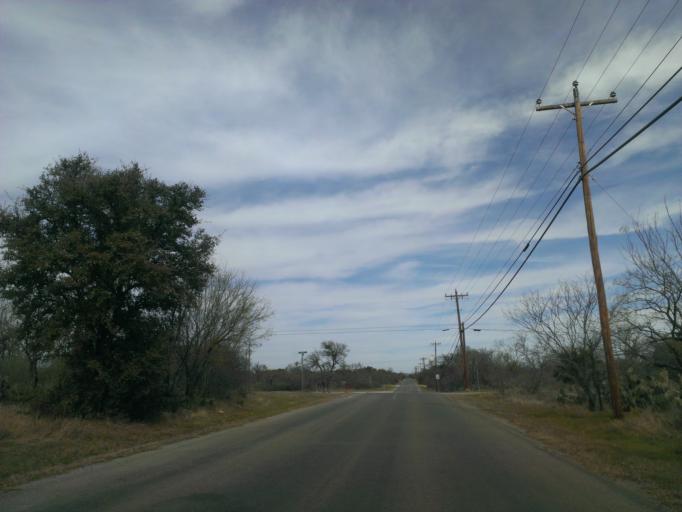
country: US
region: Texas
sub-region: Burnet County
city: Granite Shoals
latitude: 30.5794
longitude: -98.3934
